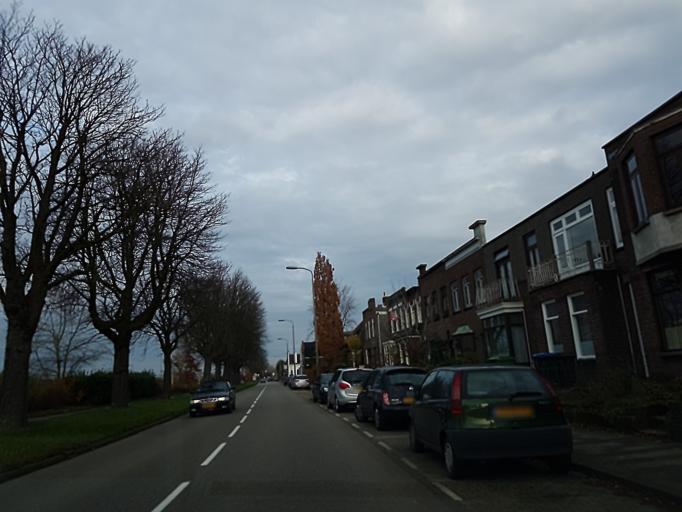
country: NL
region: North Brabant
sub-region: Roosendaal
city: Roosendaal
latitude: 51.5416
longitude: 4.4632
